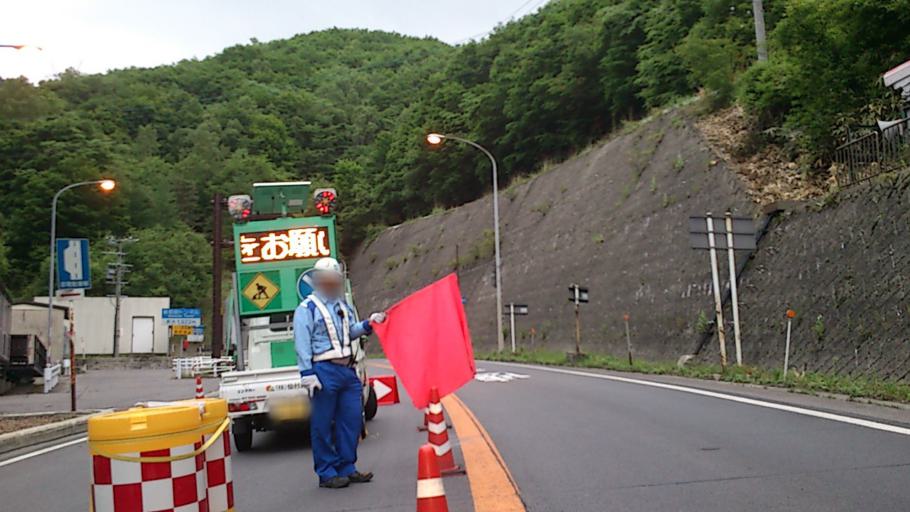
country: JP
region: Nagano
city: Suwa
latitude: 36.1435
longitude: 138.1582
